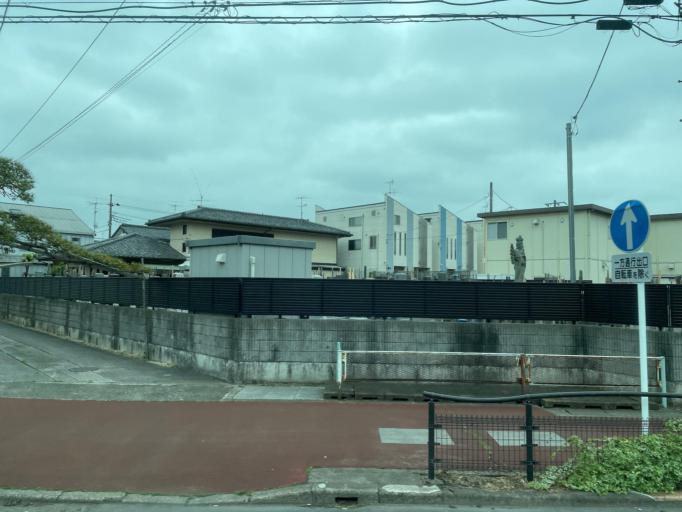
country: JP
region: Saitama
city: Iwatsuki
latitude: 35.9459
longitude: 139.6997
